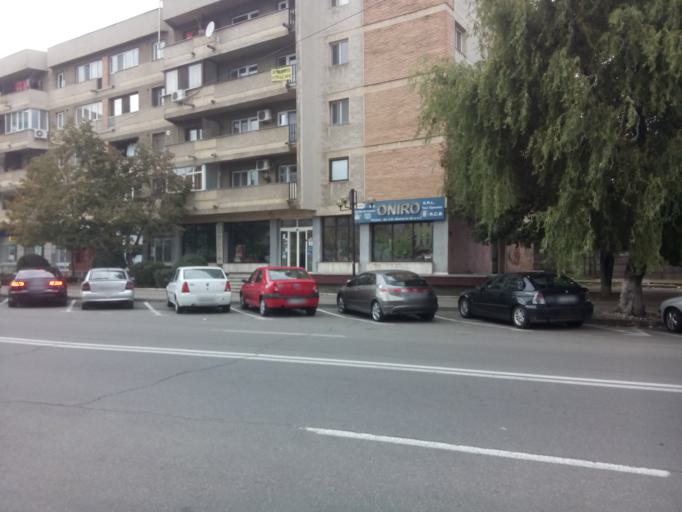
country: RO
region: Prahova
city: Ploiesti
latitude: 44.9416
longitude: 26.0275
